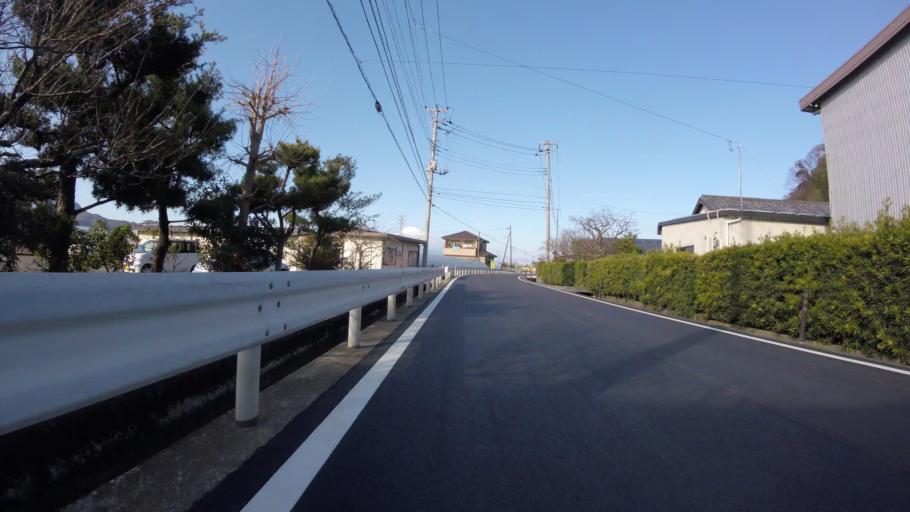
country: JP
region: Shizuoka
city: Mishima
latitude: 35.0491
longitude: 138.9526
